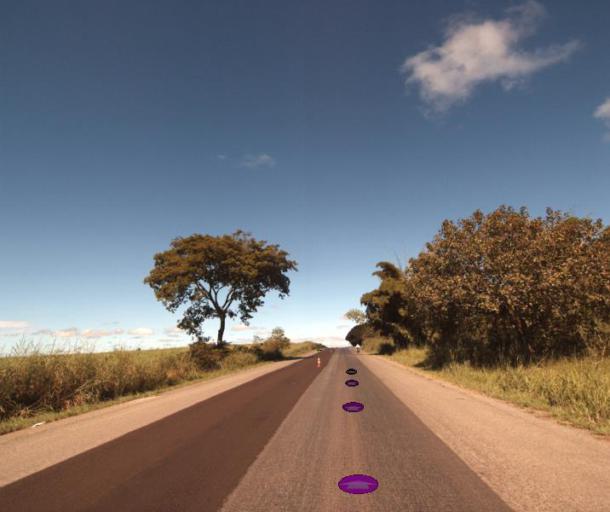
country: BR
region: Goias
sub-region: Itapaci
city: Itapaci
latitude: -15.1072
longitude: -49.4834
